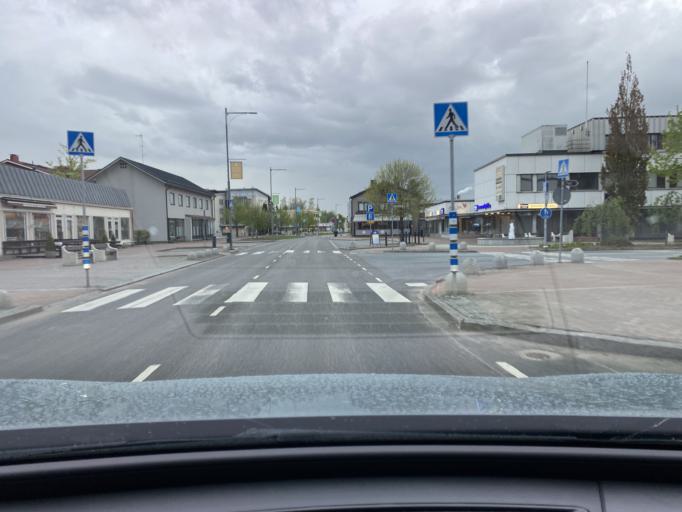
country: FI
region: Varsinais-Suomi
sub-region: Salo
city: Somero
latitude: 60.6299
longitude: 23.5137
